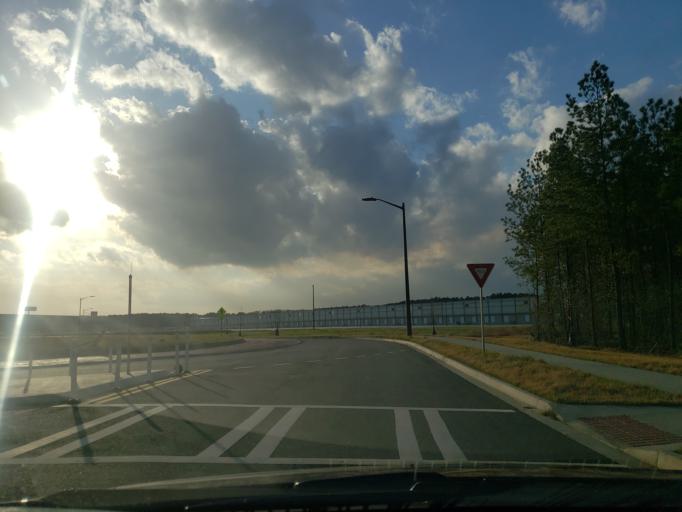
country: US
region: Georgia
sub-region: Chatham County
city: Bloomingdale
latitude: 32.1758
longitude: -81.2672
